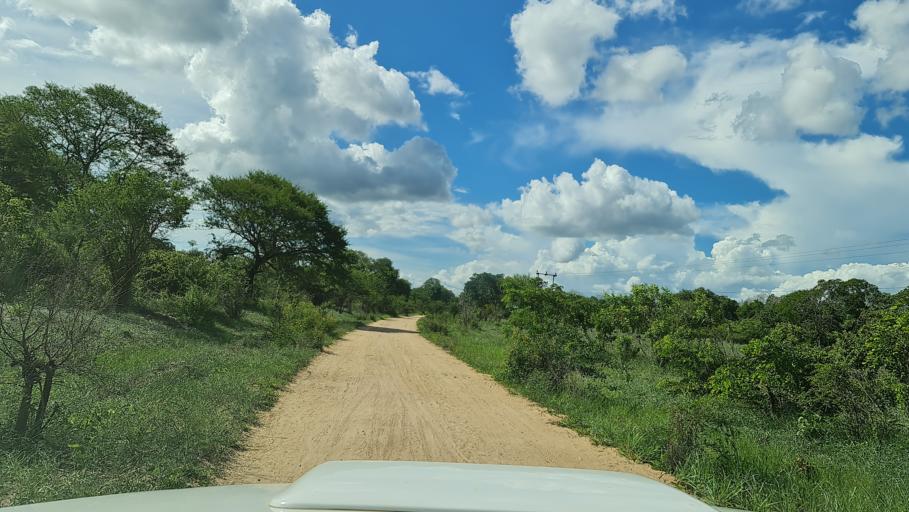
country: MZ
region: Nampula
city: Ilha de Mocambique
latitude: -15.4028
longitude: 40.2381
